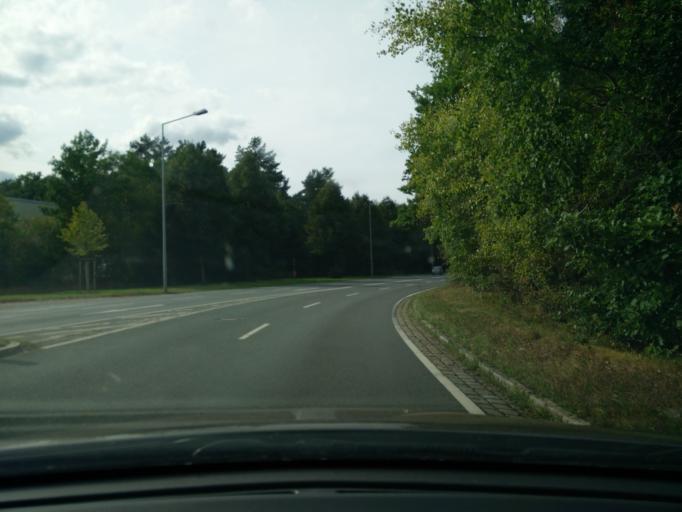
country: DE
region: Bavaria
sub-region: Regierungsbezirk Mittelfranken
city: Wendelstein
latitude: 49.4155
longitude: 11.1391
